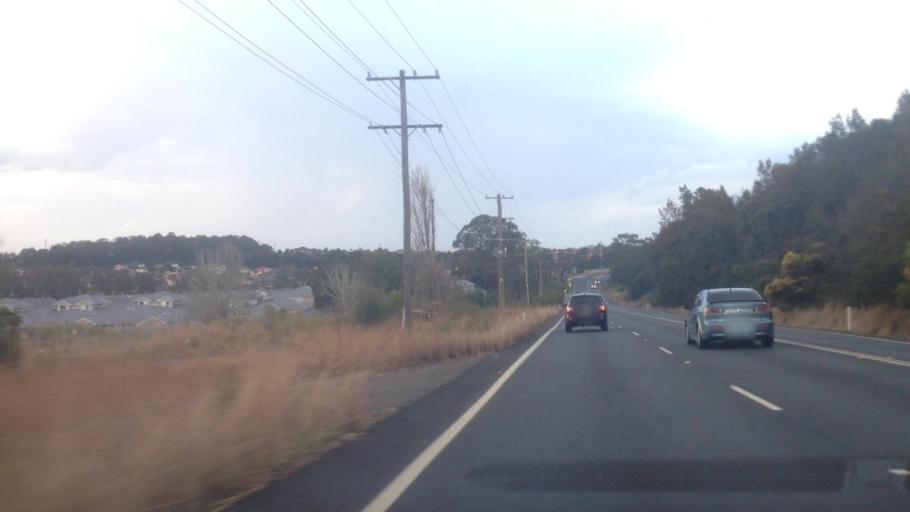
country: AU
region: New South Wales
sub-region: Wyong Shire
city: Kanwal
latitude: -33.2573
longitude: 151.4861
